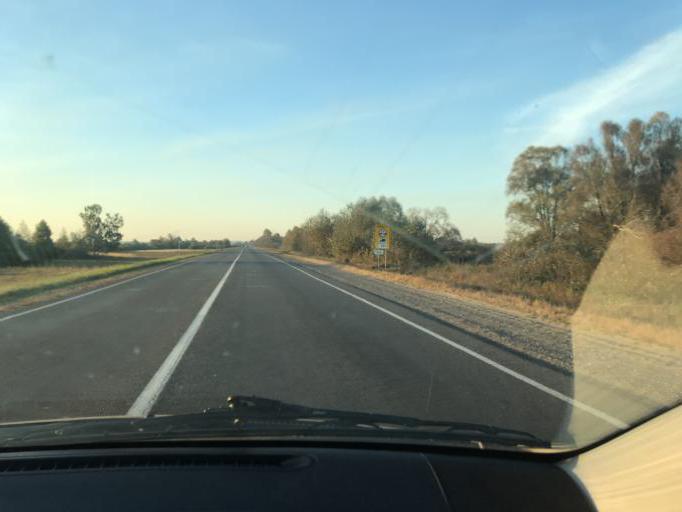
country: BY
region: Brest
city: Pinsk
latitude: 52.0814
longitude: 26.1414
